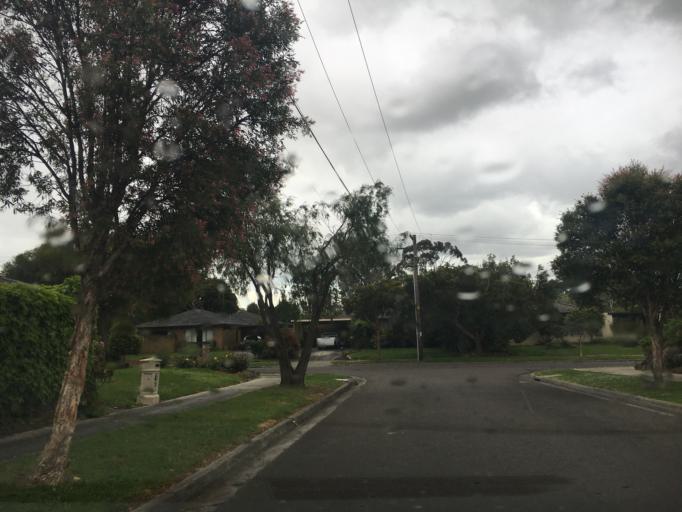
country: AU
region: Victoria
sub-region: Whitehorse
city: Vermont South
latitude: -37.8751
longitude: 145.1832
